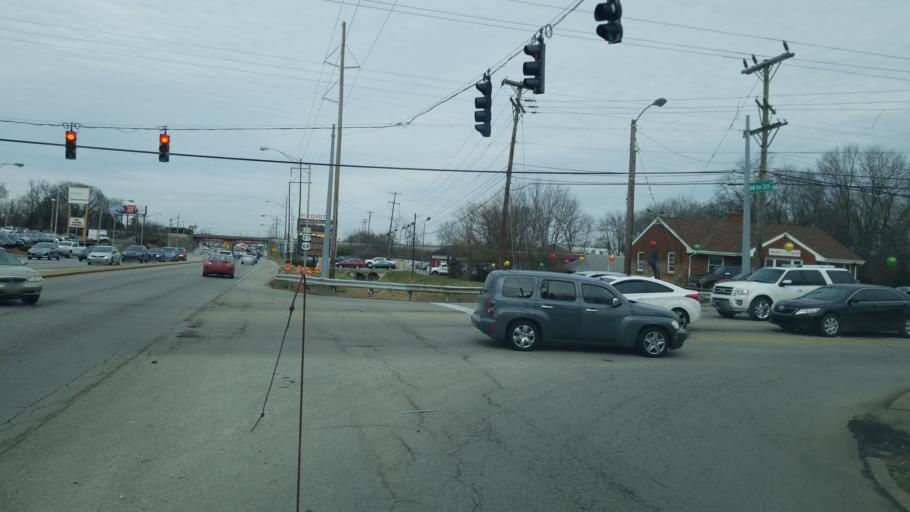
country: US
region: Kentucky
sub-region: Fayette County
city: Lexington-Fayette
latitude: 38.0652
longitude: -84.4699
